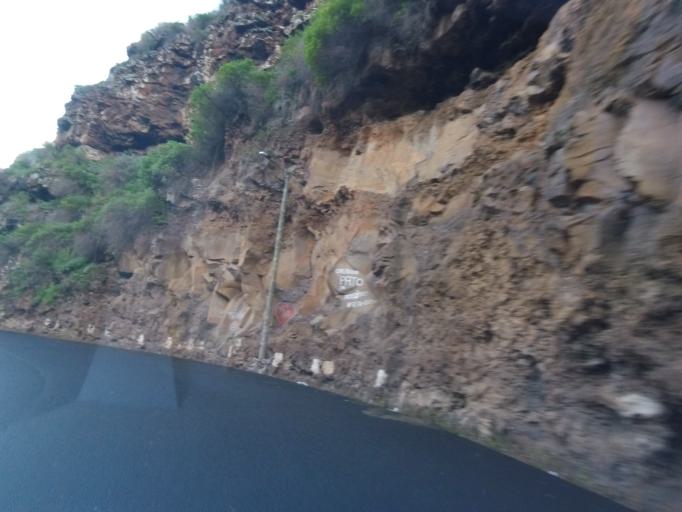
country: PT
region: Madeira
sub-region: Machico
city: Machico
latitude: 32.7038
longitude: -16.7727
